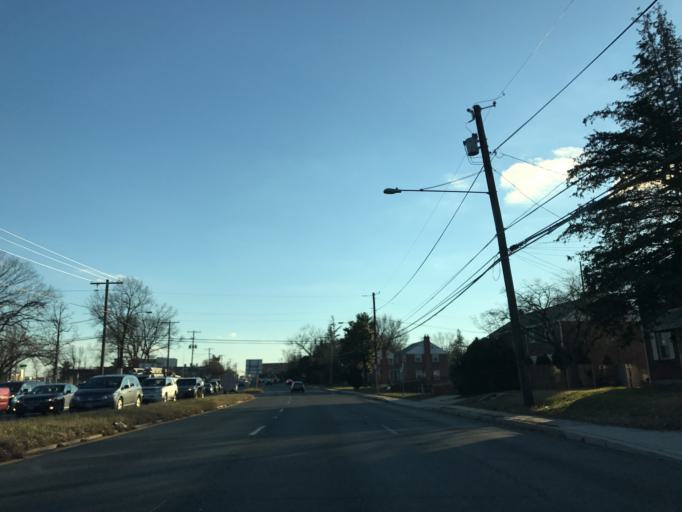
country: US
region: Maryland
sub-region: Montgomery County
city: Glenmont
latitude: 39.0502
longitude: -77.0518
